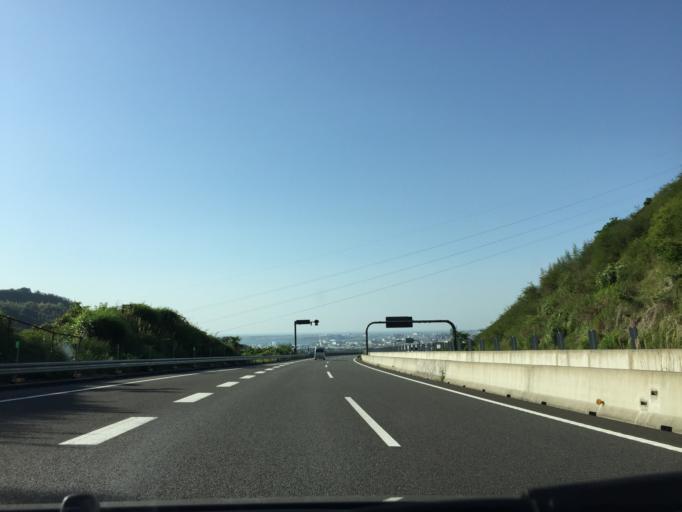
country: JP
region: Shizuoka
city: Shizuoka-shi
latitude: 35.0659
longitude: 138.4803
